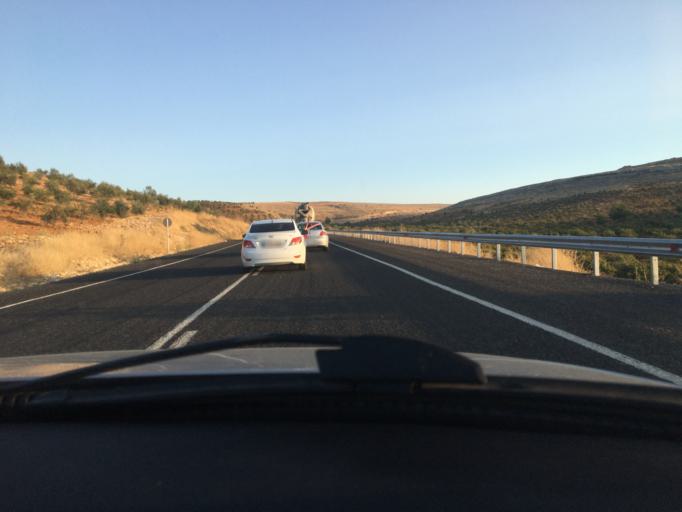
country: TR
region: Sanliurfa
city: Halfeti
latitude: 37.1913
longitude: 37.9690
